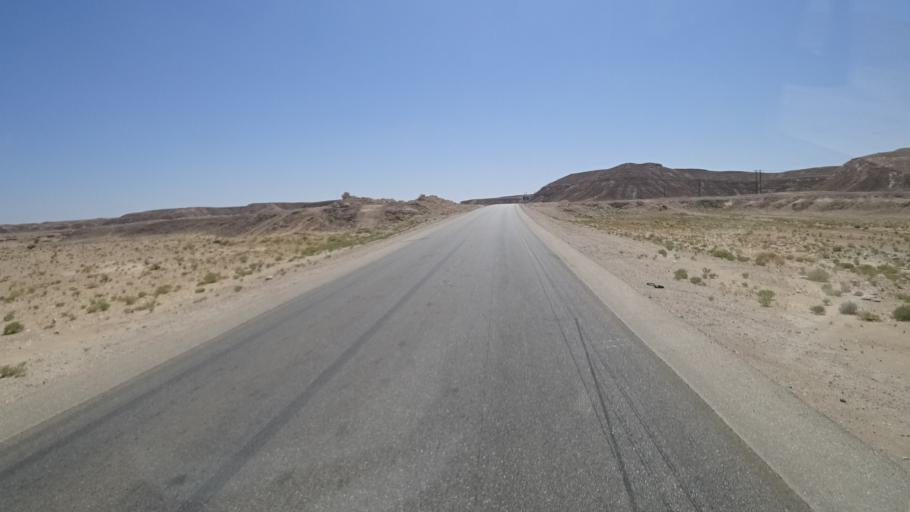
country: OM
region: Zufar
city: Salalah
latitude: 17.5033
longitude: 53.3632
